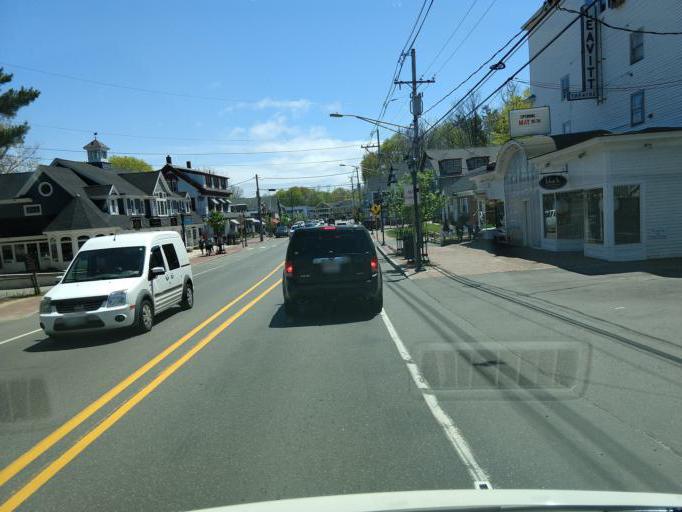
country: US
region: Maine
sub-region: York County
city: Ogunquit
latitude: 43.2528
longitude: -70.6008
